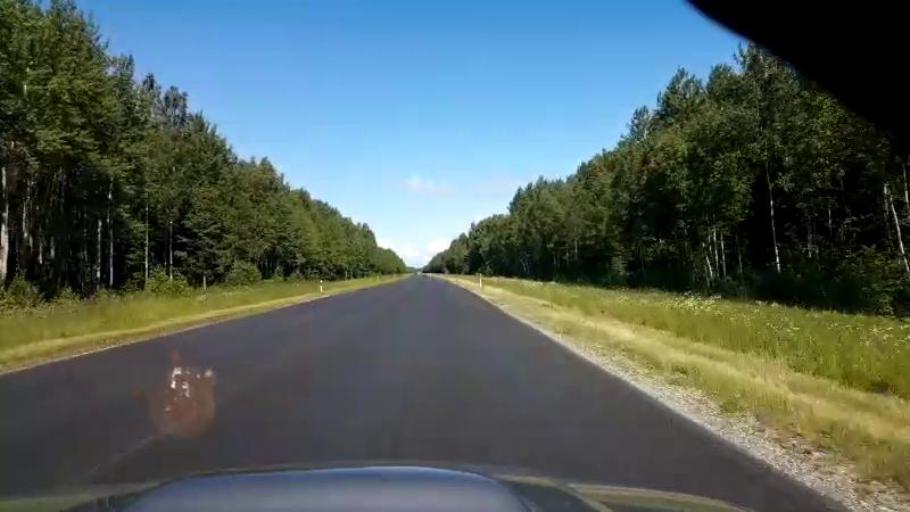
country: LV
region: Salacgrivas
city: Ainazi
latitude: 57.9168
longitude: 24.4212
